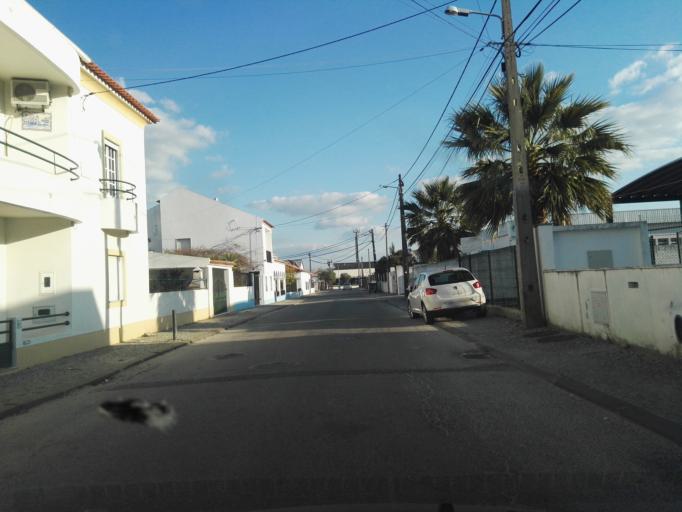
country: PT
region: Evora
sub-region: Evora
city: Evora
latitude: 38.5615
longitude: -7.9241
